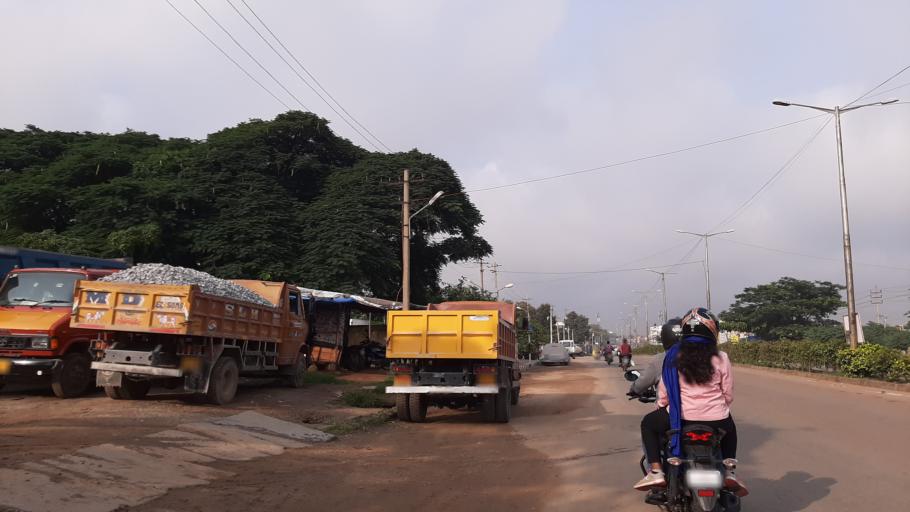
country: IN
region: Karnataka
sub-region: Bangalore Urban
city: Bangalore
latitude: 12.9871
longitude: 77.4920
